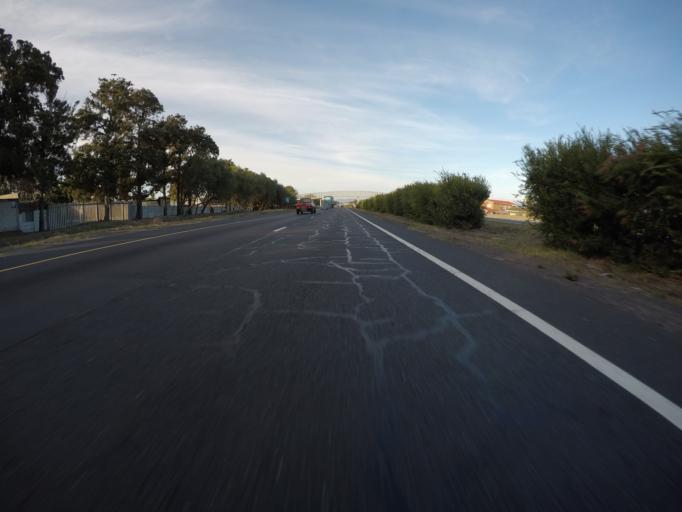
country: ZA
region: Western Cape
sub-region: City of Cape Town
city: Kraaifontein
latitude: -33.8497
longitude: 18.7081
